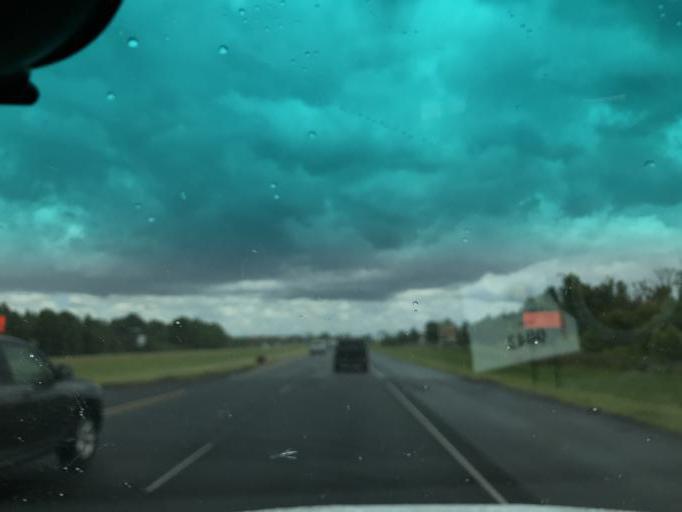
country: US
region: Alabama
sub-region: Montgomery County
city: Pike Road
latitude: 32.3640
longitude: -86.1560
